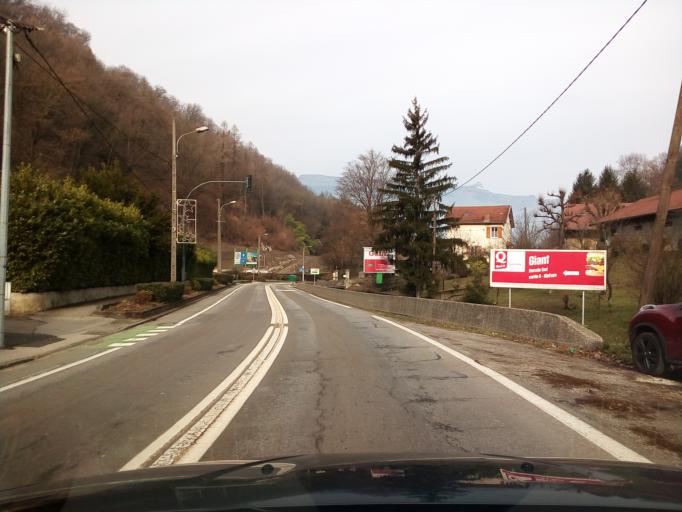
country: FR
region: Rhone-Alpes
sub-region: Departement de l'Isere
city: Gieres
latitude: 45.1751
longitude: 5.7901
